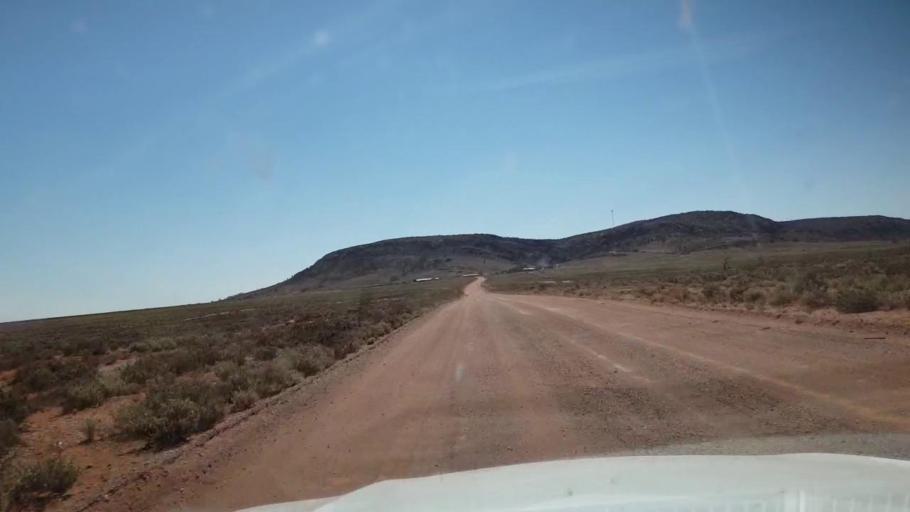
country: AU
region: South Australia
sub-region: Whyalla
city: Whyalla
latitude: -32.6951
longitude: 137.1310
